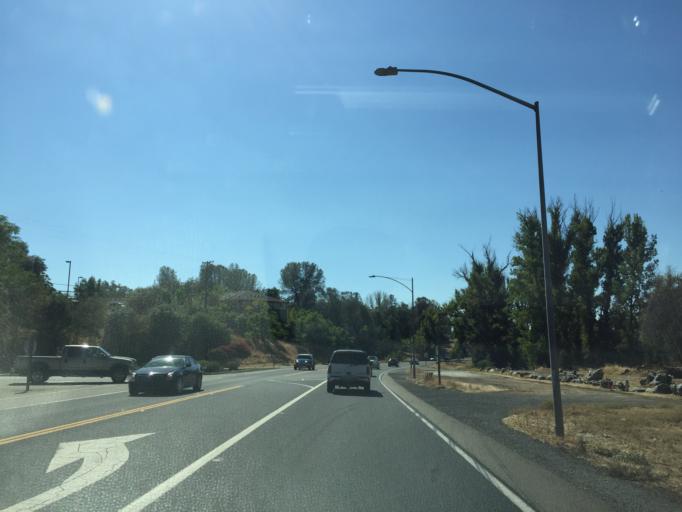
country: US
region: California
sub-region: Tuolumne County
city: Jamestown
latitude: 37.9516
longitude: -120.4248
